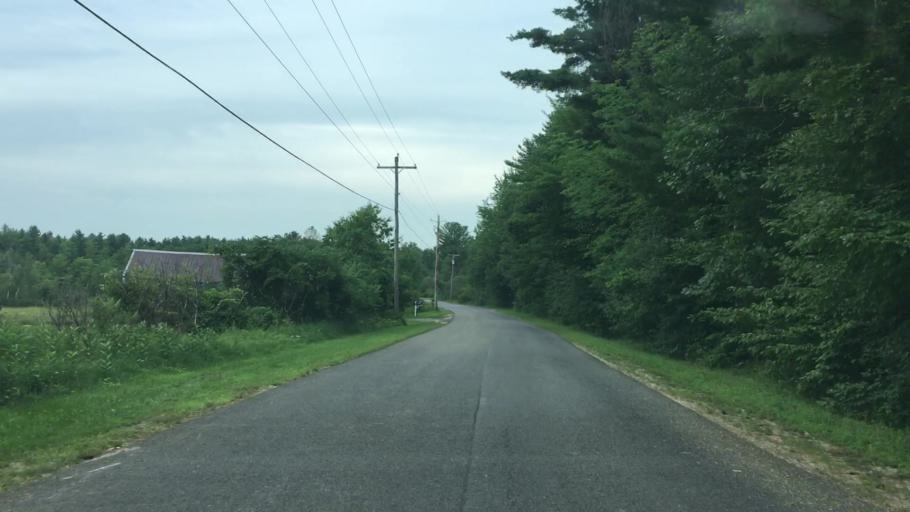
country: US
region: New York
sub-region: Clinton County
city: Peru
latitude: 44.6027
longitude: -73.6069
